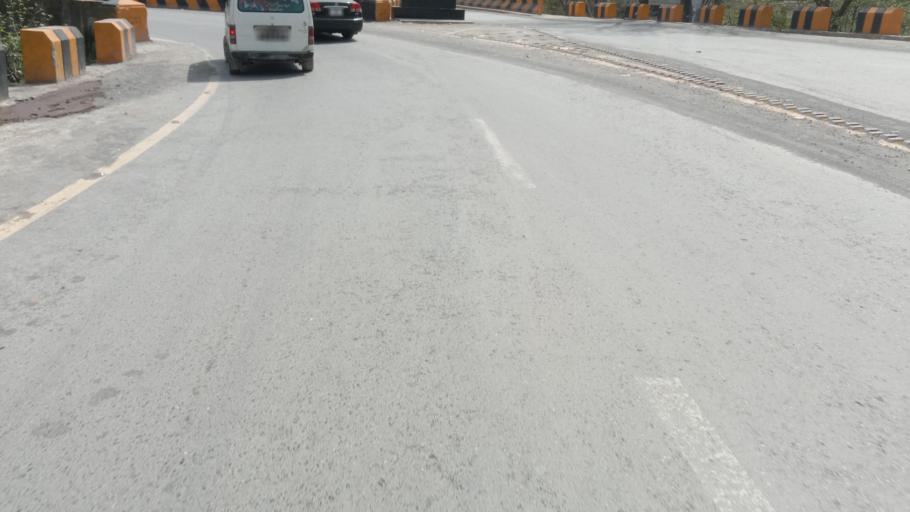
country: PK
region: Khyber Pakhtunkhwa
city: Abbottabad
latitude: 34.1511
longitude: 73.2669
